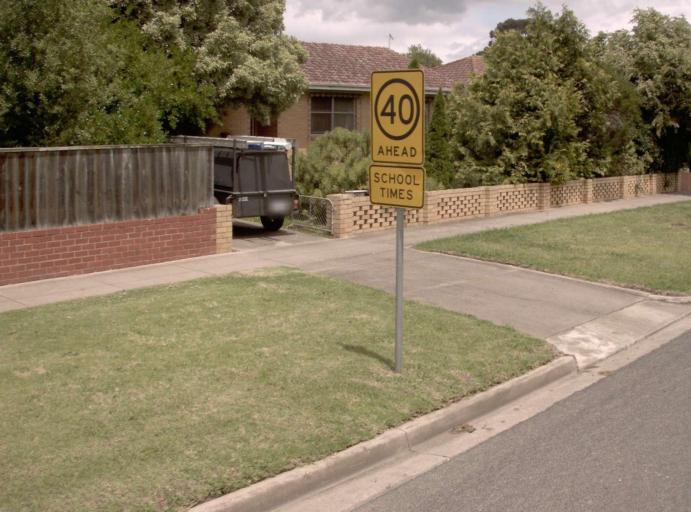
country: AU
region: Victoria
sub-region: Wellington
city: Sale
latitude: -38.1008
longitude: 147.0869
